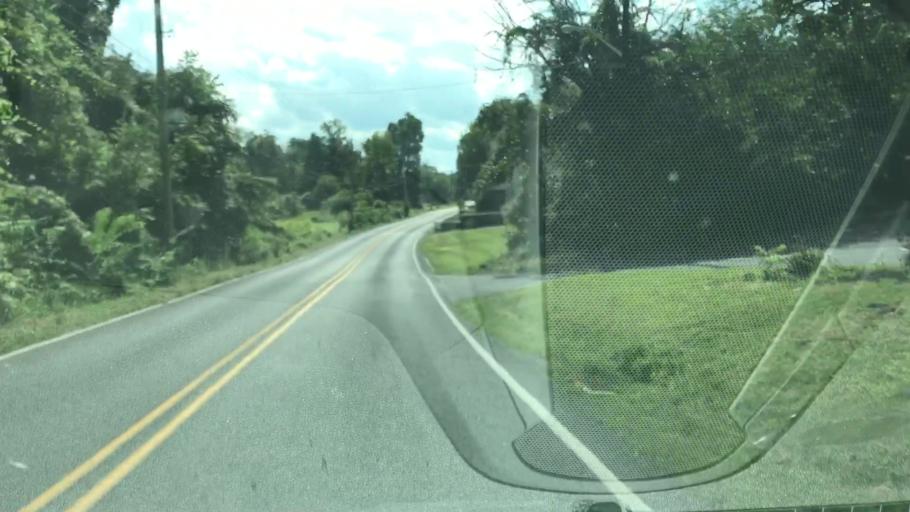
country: US
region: Pennsylvania
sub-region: Dauphin County
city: Middletown
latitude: 40.1815
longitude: -76.6958
